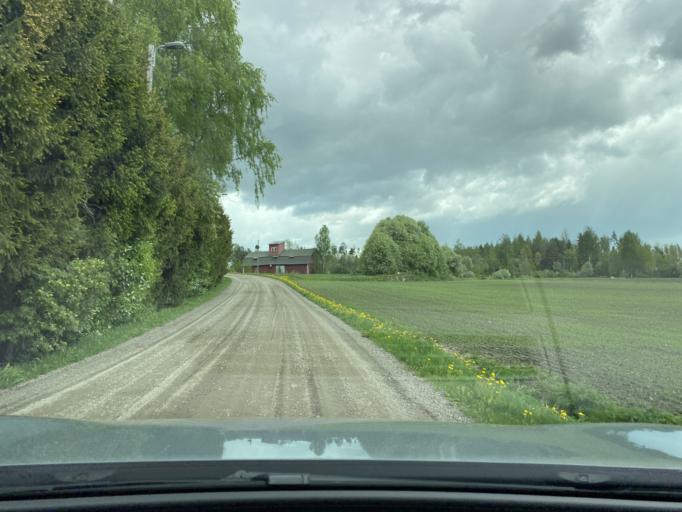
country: FI
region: Uusimaa
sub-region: Porvoo
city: Pukkila
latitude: 60.7614
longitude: 25.4339
